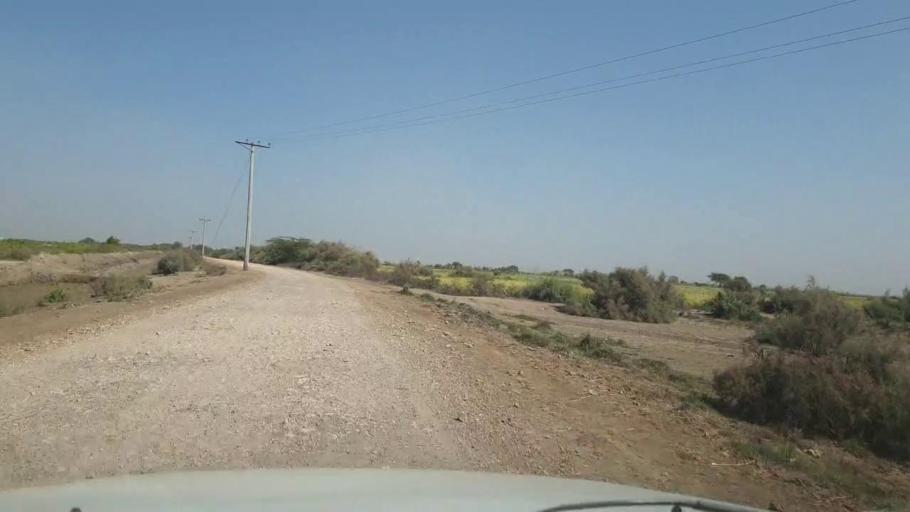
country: PK
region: Sindh
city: Mirpur Sakro
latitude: 24.4002
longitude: 67.7592
